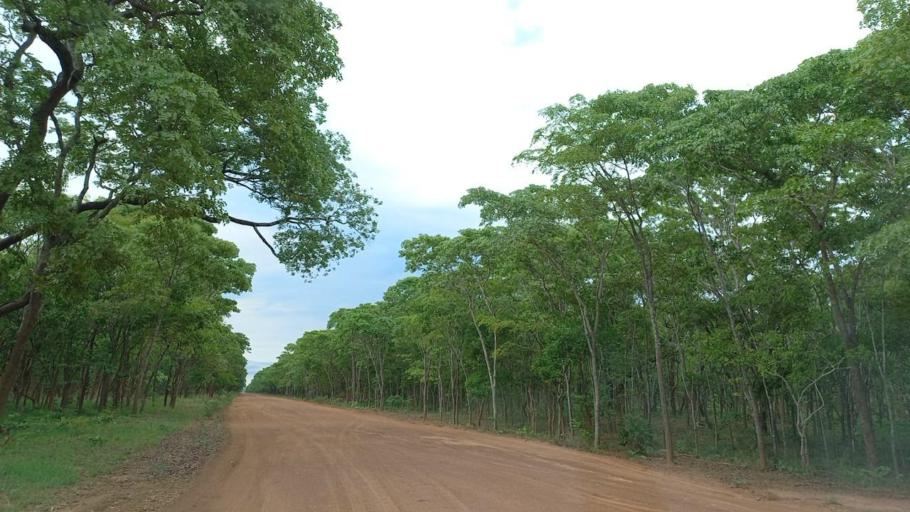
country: ZM
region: North-Western
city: Kalengwa
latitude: -13.3568
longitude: 25.0766
